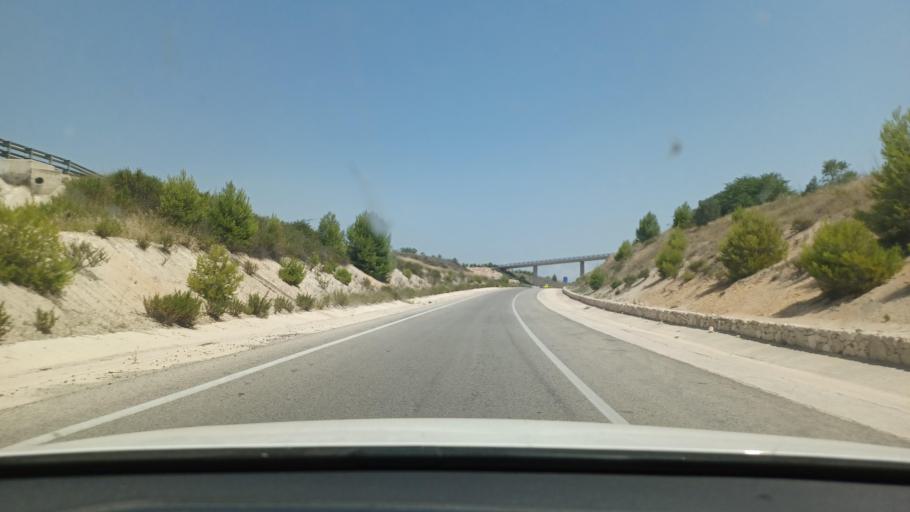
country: ES
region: Valencia
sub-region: Provincia de Alicante
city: Alcoy
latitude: 38.6841
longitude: -0.4607
